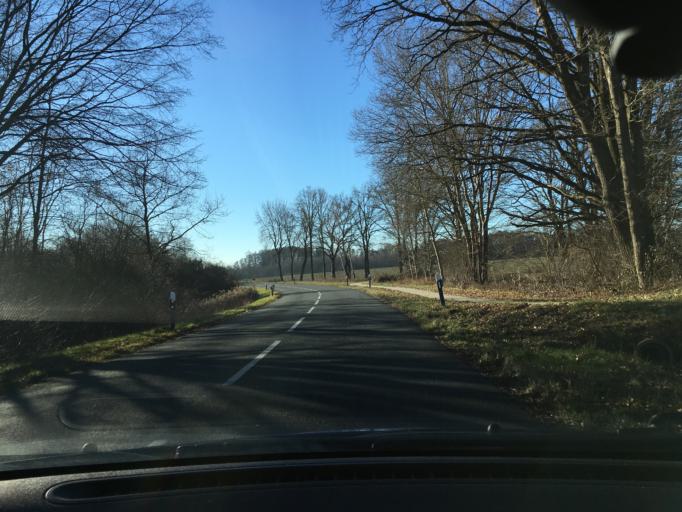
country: DE
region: Lower Saxony
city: Melbeck
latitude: 53.1727
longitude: 10.3809
